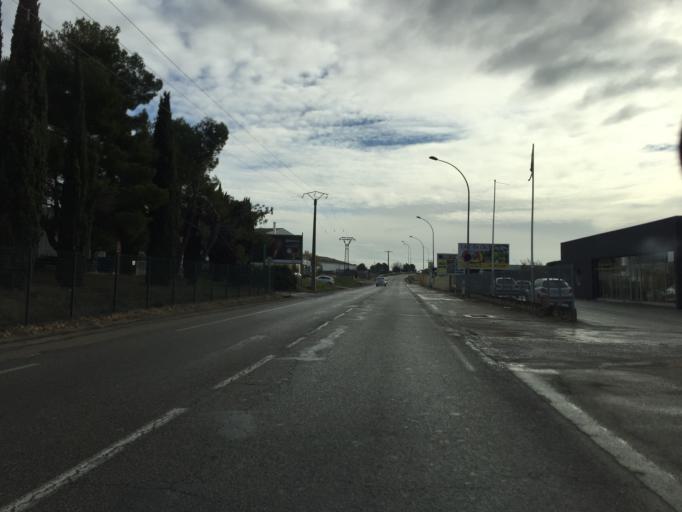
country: FR
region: Provence-Alpes-Cote d'Azur
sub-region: Departement du Vaucluse
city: Sorgues
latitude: 44.0122
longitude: 4.8860
